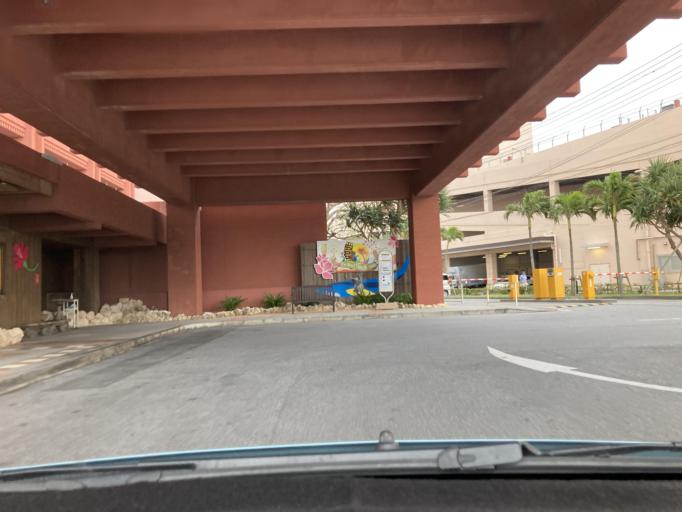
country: JP
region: Okinawa
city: Chatan
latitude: 26.3136
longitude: 127.7566
